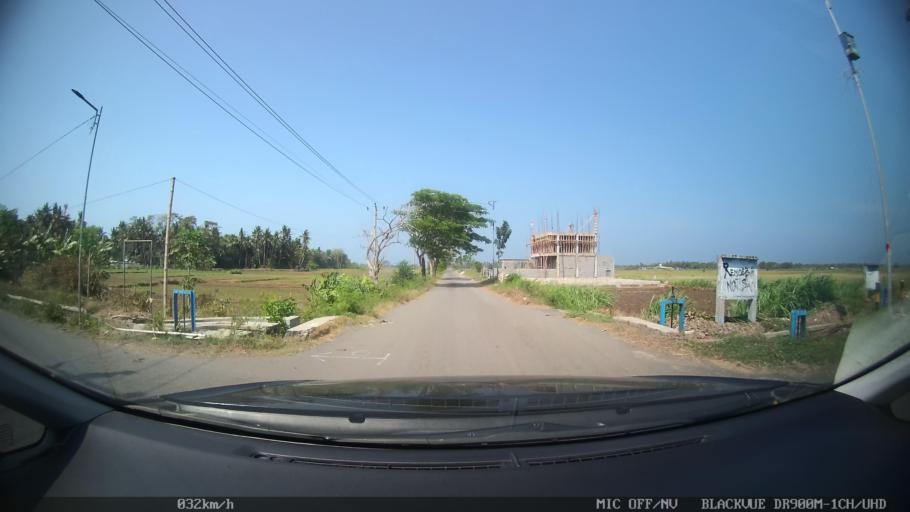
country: ID
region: Daerah Istimewa Yogyakarta
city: Srandakan
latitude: -7.9652
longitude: 110.2133
